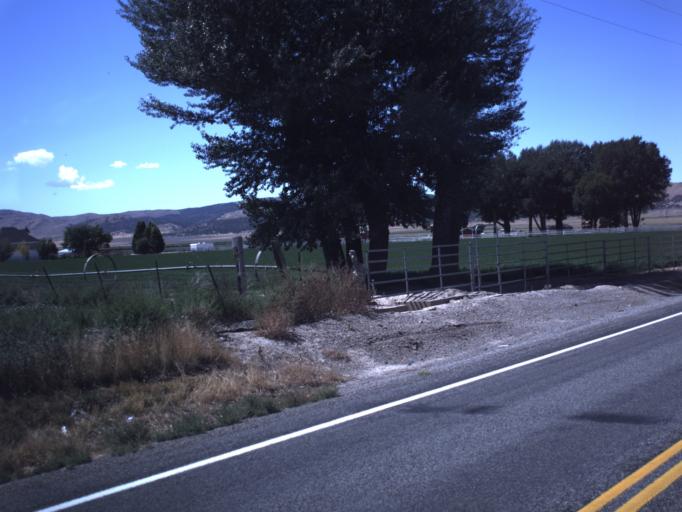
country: US
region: Utah
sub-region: Juab County
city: Nephi
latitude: 39.7101
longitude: -111.8747
